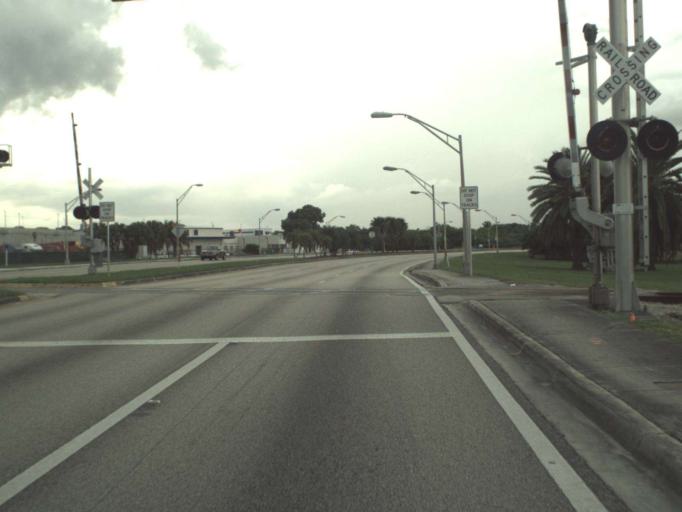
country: US
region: Florida
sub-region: Miami-Dade County
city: Flagami
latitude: 25.7841
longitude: -80.3186
